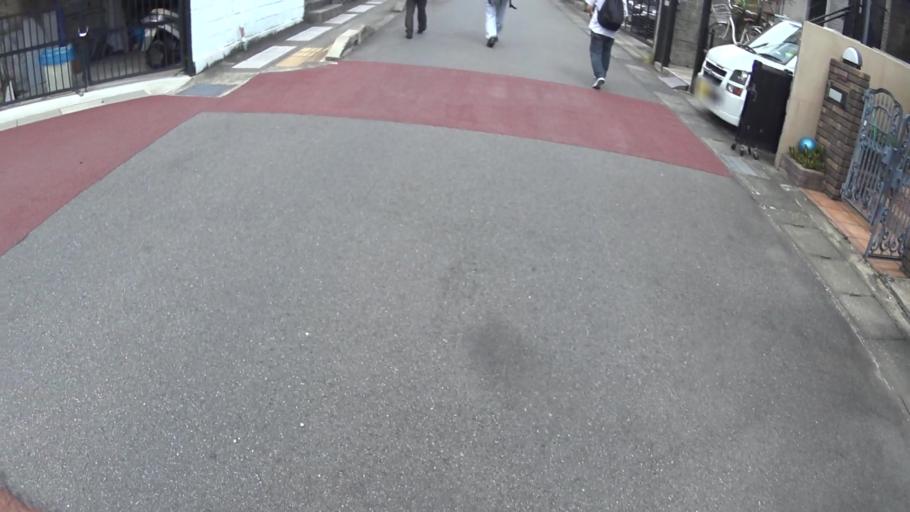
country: JP
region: Kyoto
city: Yawata
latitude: 34.9083
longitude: 135.6965
